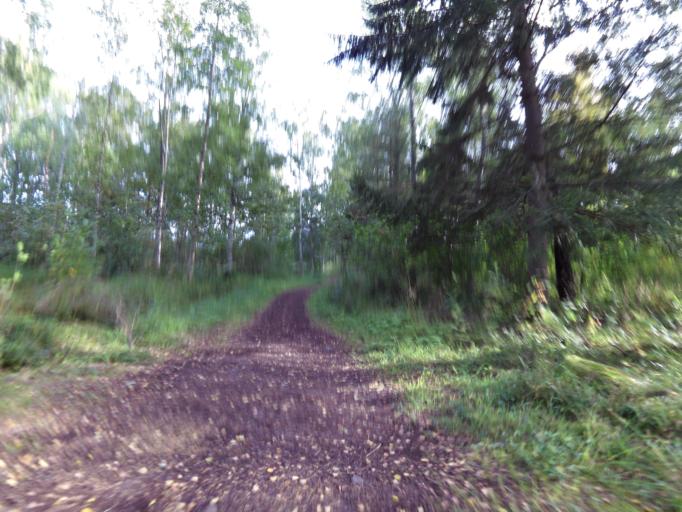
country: SE
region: Gaevleborg
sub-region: Gavle Kommun
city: Gavle
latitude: 60.6829
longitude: 17.2398
